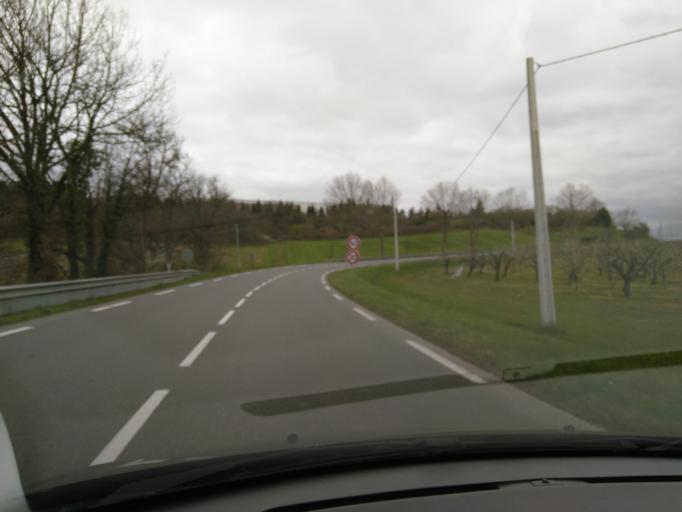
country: FR
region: Aquitaine
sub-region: Departement du Lot-et-Garonne
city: Cancon
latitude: 44.4898
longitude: 0.6684
